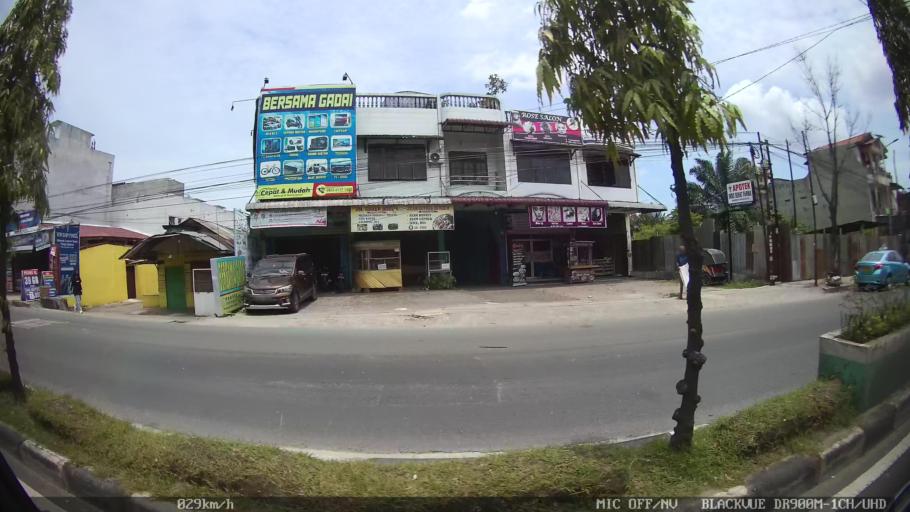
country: ID
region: North Sumatra
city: Sunggal
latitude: 3.5440
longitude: 98.6247
